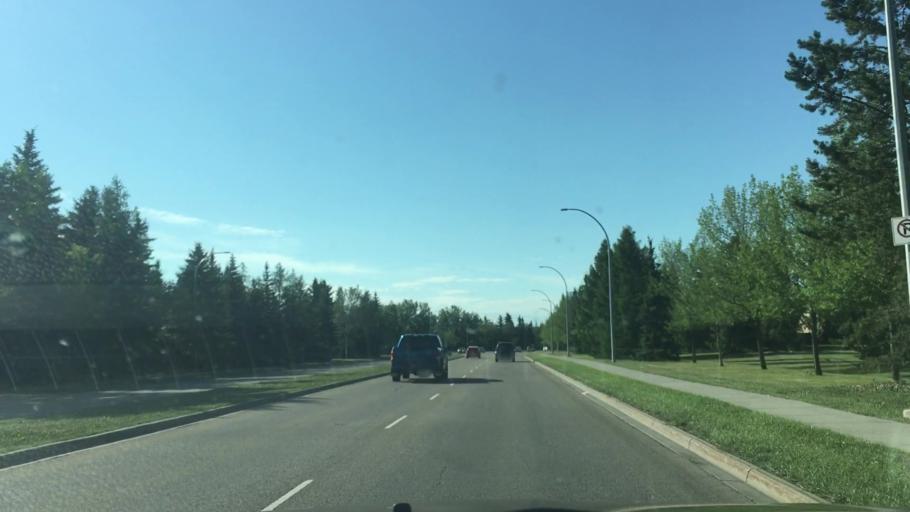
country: CA
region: Alberta
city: Edmonton
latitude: 53.4581
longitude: -113.5366
